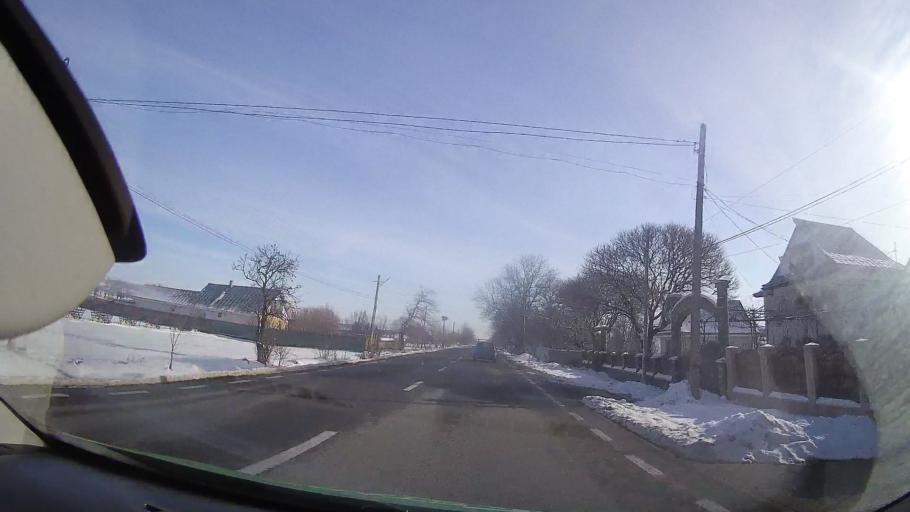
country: RO
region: Neamt
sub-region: Comuna Negresti
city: Negresti
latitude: 47.0590
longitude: 26.3879
